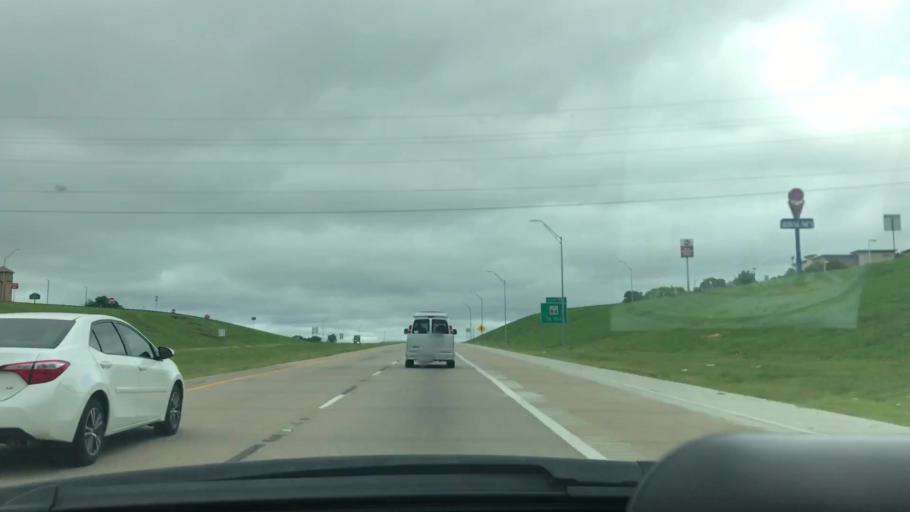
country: US
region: Texas
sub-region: Grayson County
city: Denison
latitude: 33.7625
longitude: -96.5852
